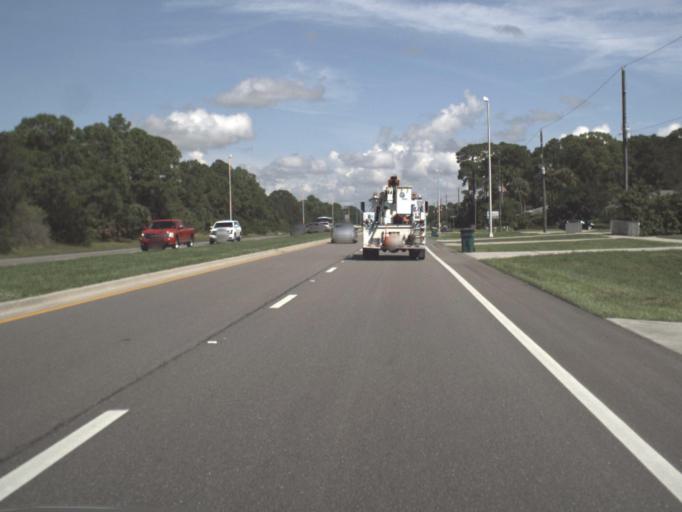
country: US
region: Florida
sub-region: Sarasota County
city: North Port
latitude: 27.0261
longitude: -82.1636
